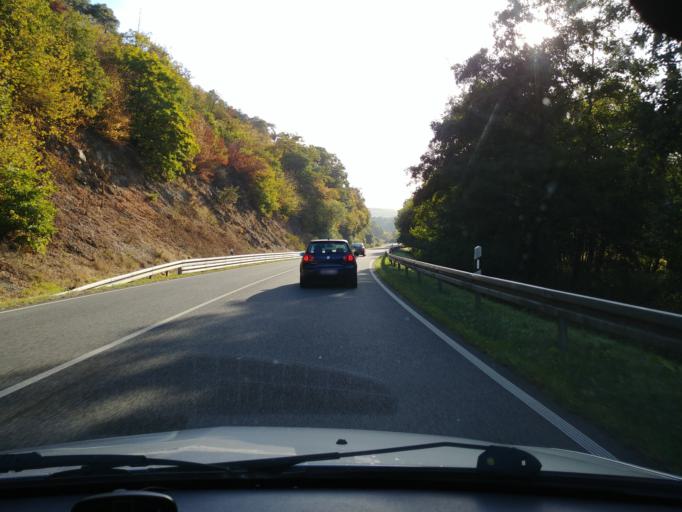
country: DE
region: Hesse
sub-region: Regierungsbezirk Darmstadt
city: Usingen
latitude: 50.3564
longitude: 8.5808
